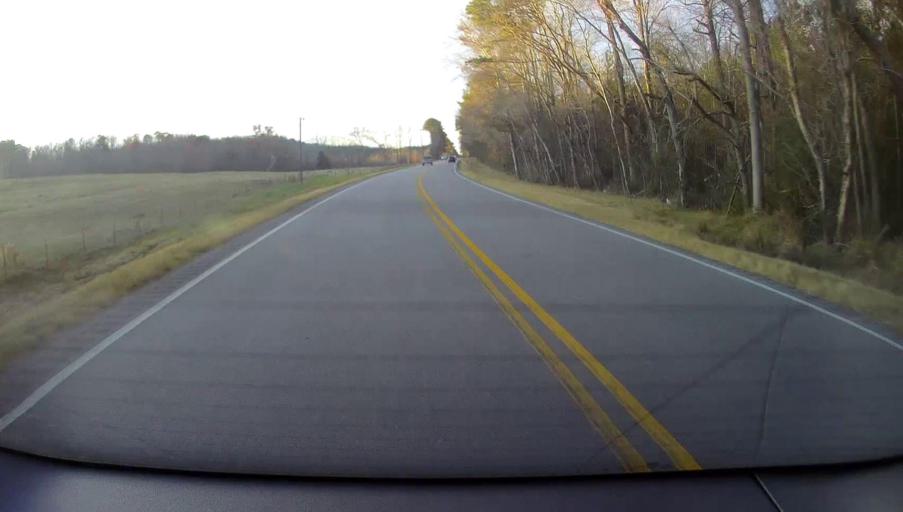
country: US
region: Alabama
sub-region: Saint Clair County
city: Steele
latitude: 34.0730
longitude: -86.3294
